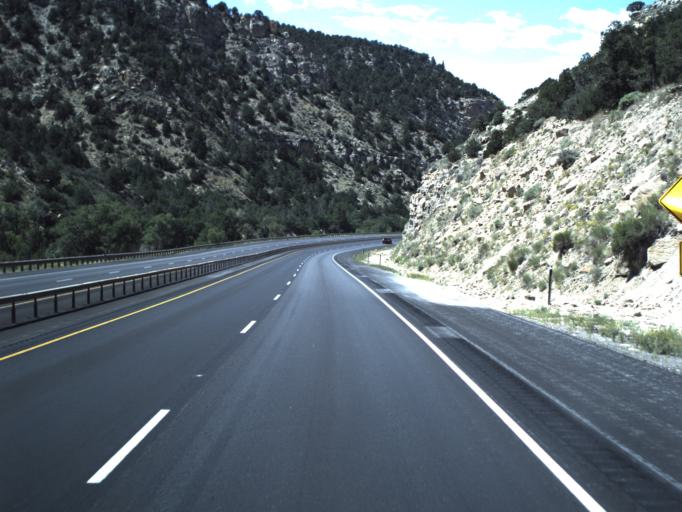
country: US
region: Utah
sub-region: Sevier County
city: Salina
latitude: 38.8951
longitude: -111.6249
